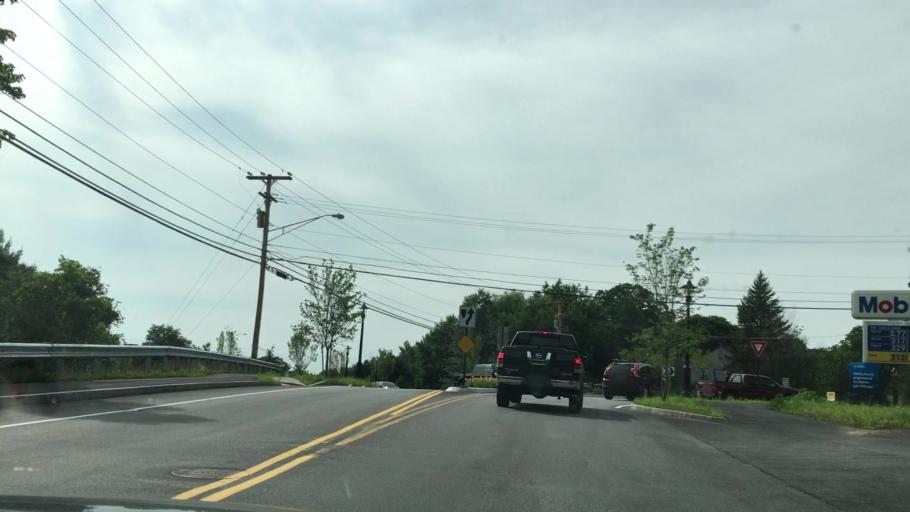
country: US
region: New Hampshire
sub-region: Merrimack County
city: East Concord
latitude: 43.2367
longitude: -71.5349
